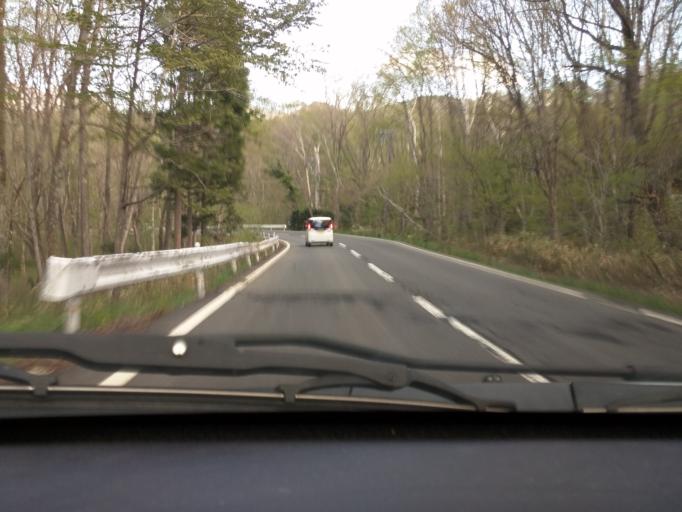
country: JP
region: Nagano
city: Nagano-shi
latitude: 36.7248
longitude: 138.0911
